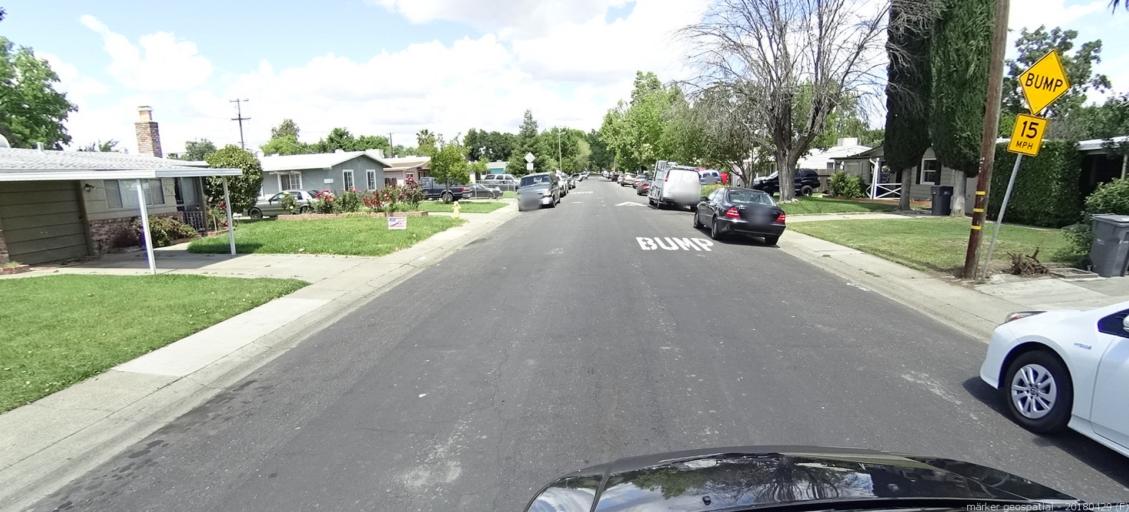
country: US
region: California
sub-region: Yolo County
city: West Sacramento
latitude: 38.5914
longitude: -121.5229
